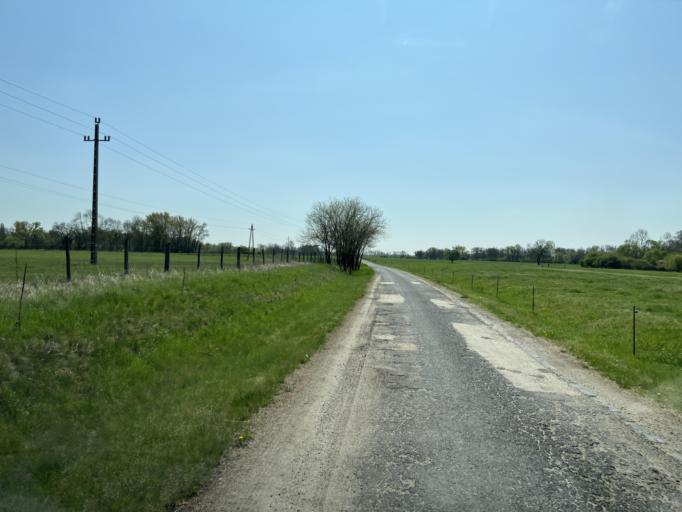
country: HU
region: Pest
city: Inarcs
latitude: 47.2606
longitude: 19.2786
